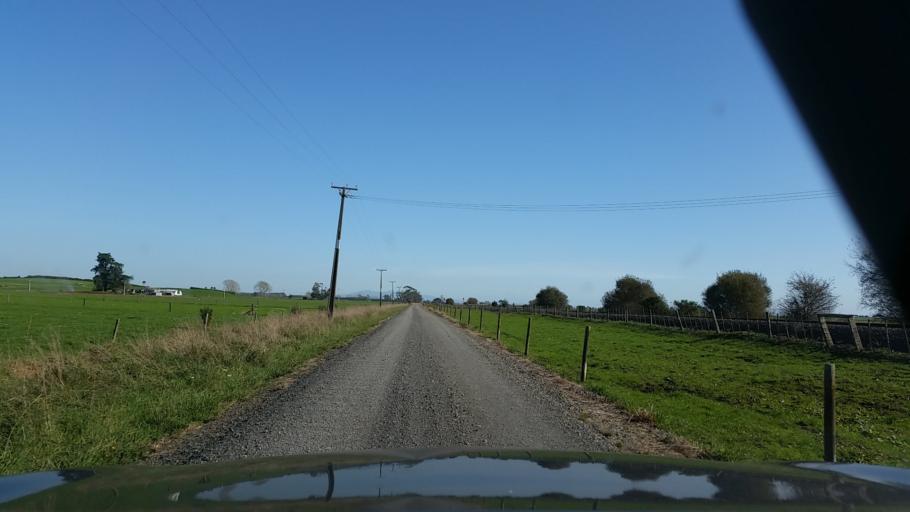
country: NZ
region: Waikato
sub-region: Waipa District
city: Cambridge
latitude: -37.6783
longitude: 175.4604
